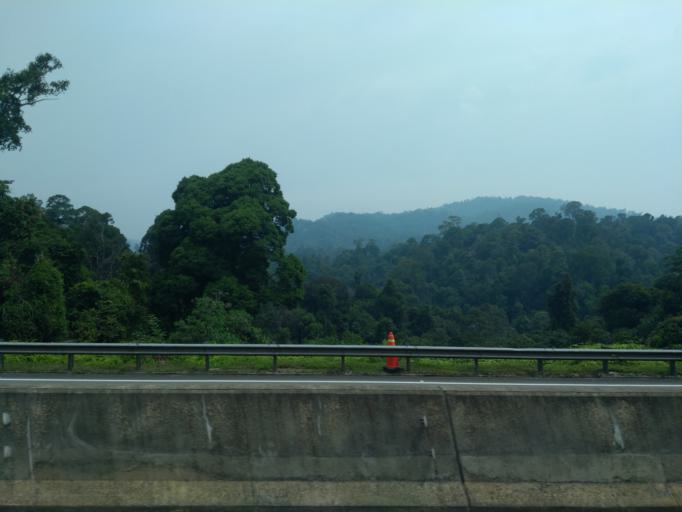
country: MY
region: Perak
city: Kuala Kangsar
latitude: 4.6864
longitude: 100.9981
